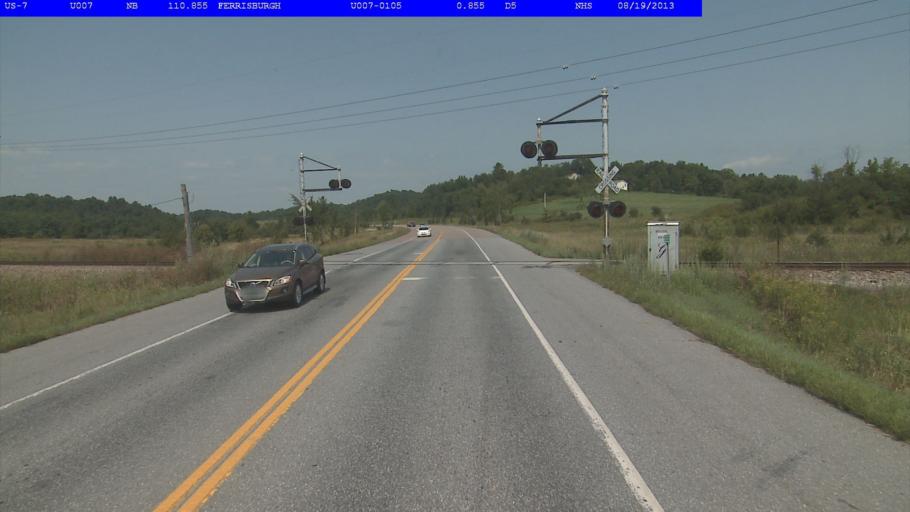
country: US
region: Vermont
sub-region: Addison County
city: Vergennes
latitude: 44.1741
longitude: -73.2394
